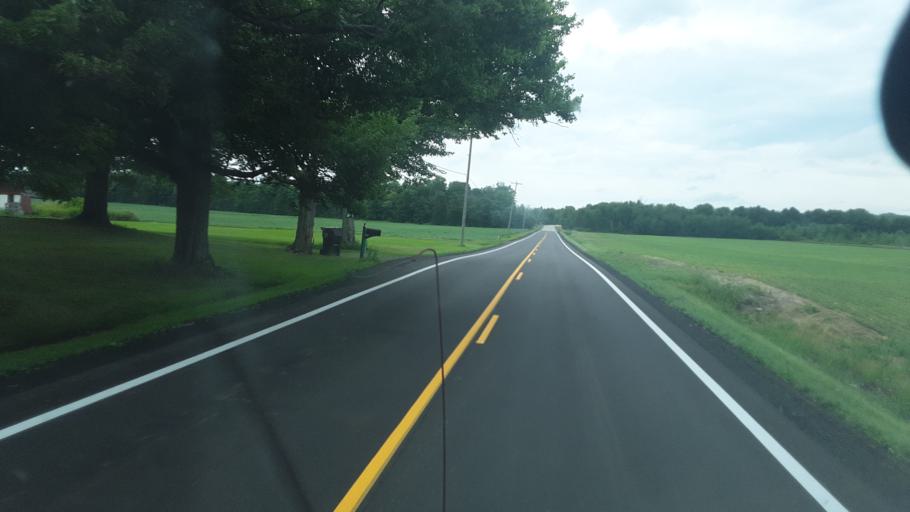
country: US
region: Ohio
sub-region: Trumbull County
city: Cortland
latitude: 41.3449
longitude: -80.6611
